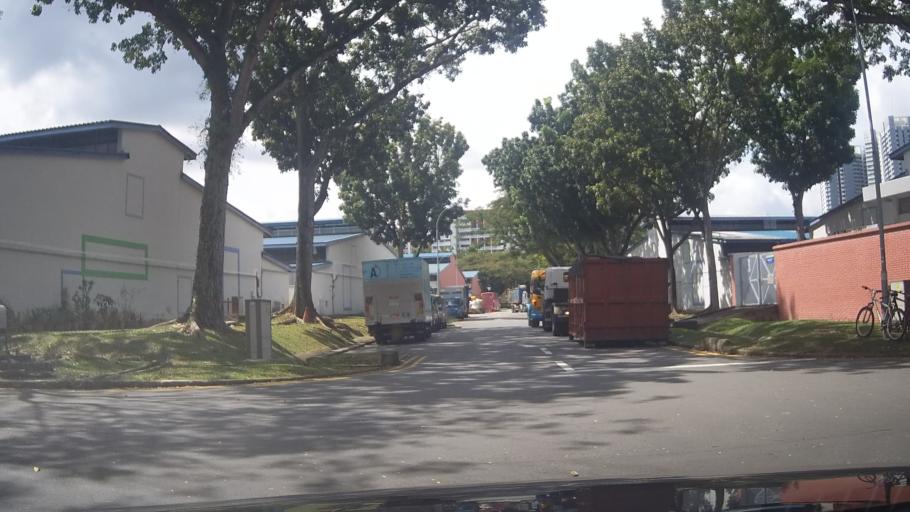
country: MY
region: Johor
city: Johor Bahru
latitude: 1.4418
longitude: 103.7826
